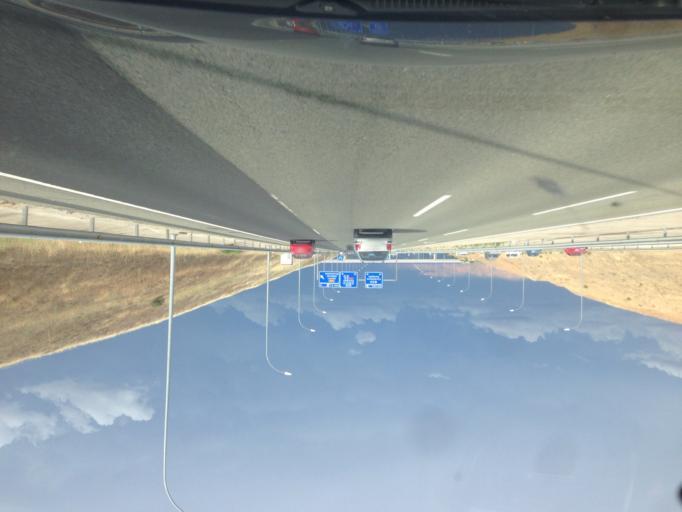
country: ES
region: Madrid
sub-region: Provincia de Madrid
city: Paracuellos de Jarama
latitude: 40.5281
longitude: -3.5162
